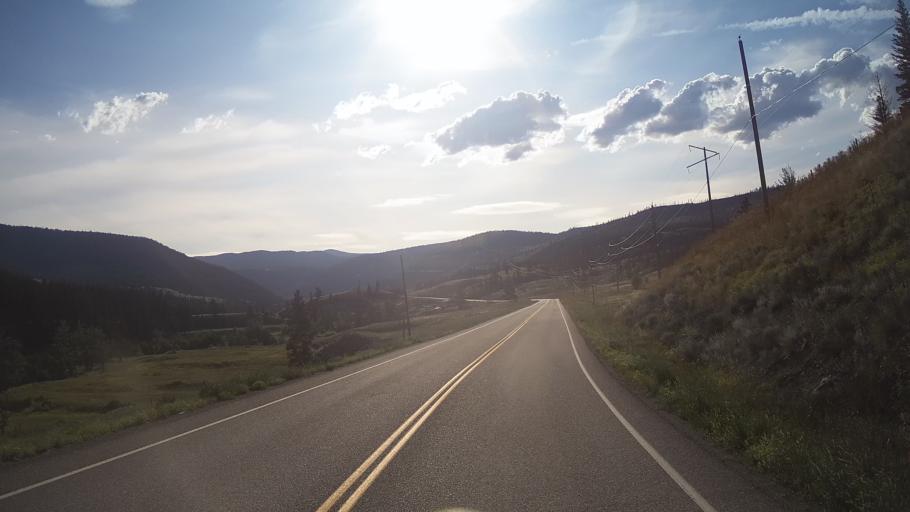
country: CA
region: British Columbia
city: Cache Creek
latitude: 50.8871
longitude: -121.4442
